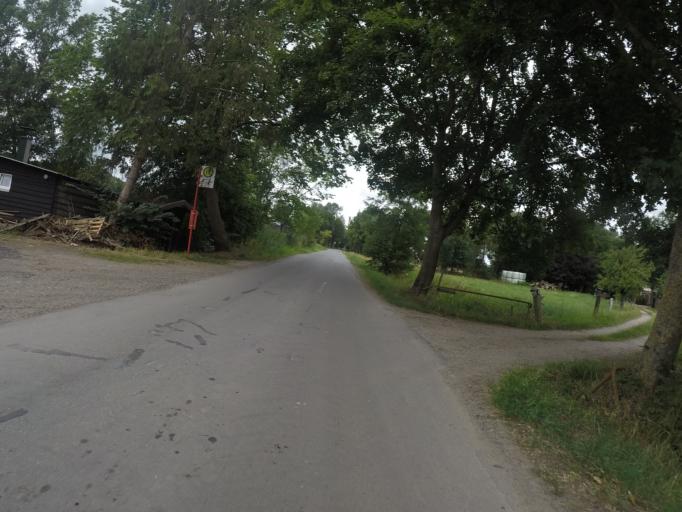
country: DE
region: Lower Saxony
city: Grossenworden
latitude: 53.6833
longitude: 9.2399
